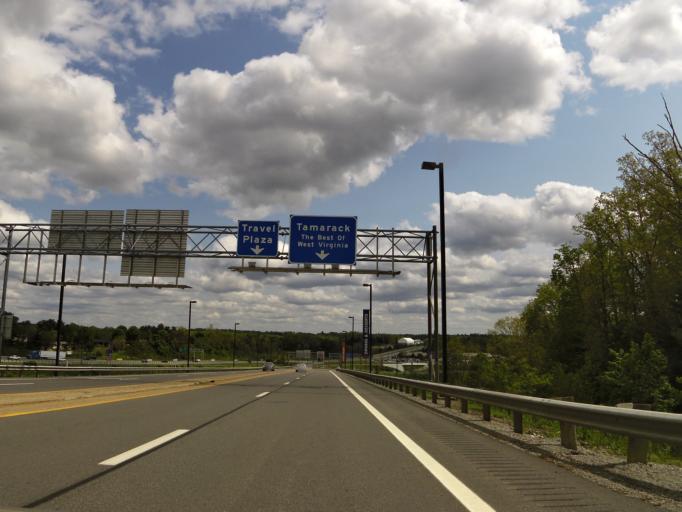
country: US
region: West Virginia
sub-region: Raleigh County
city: Prosperity
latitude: 37.8093
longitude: -81.2144
